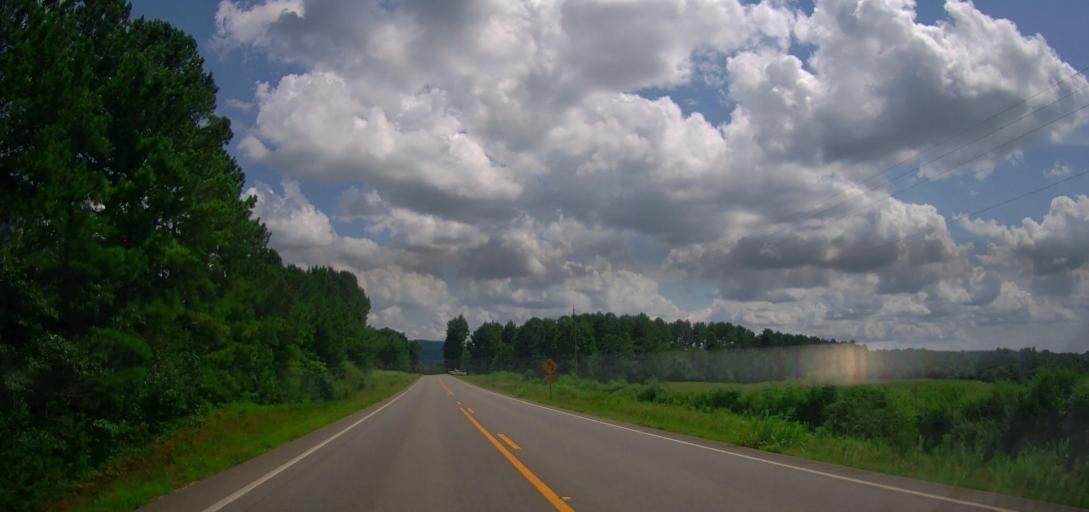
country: US
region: Alabama
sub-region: Cleburne County
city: Heflin
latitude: 33.5877
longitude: -85.4754
